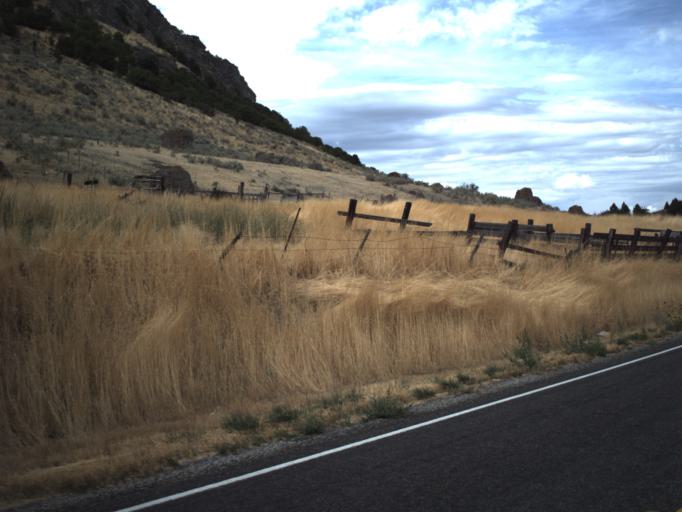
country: US
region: Utah
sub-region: Cache County
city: Benson
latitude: 41.9026
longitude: -111.9513
